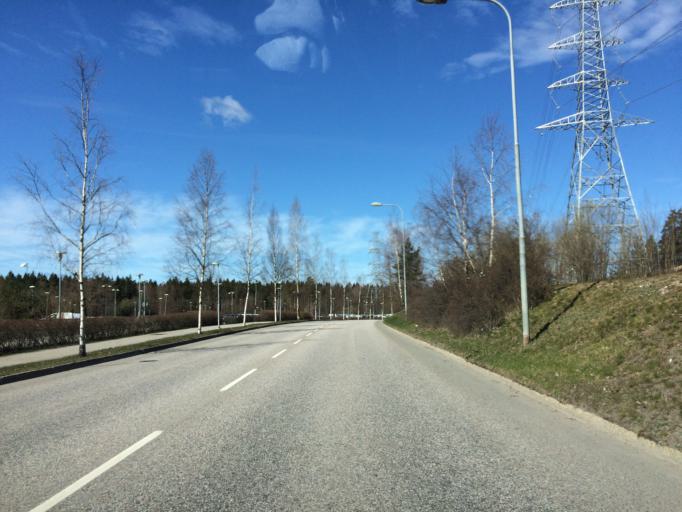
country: SE
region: Stockholm
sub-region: Stockholms Kommun
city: Kista
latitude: 59.4227
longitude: 17.9188
